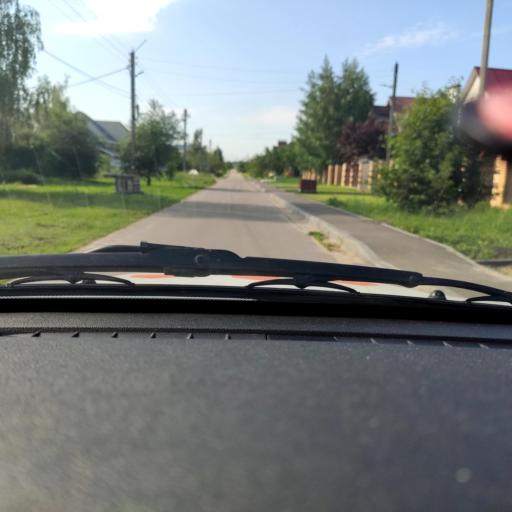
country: RU
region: Voronezj
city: Novaya Usman'
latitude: 51.6460
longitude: 39.3331
